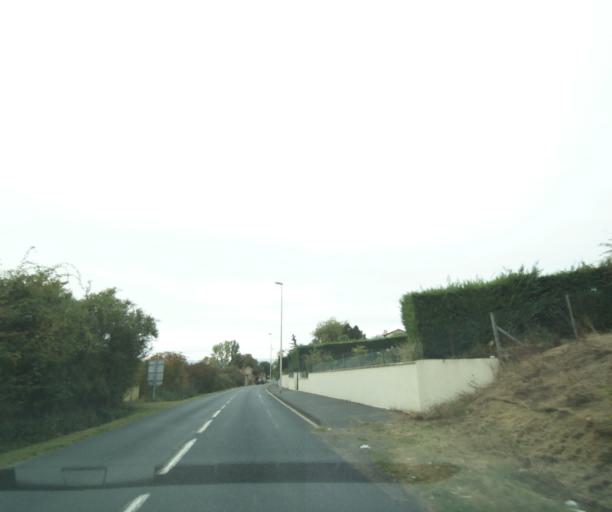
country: FR
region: Auvergne
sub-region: Departement du Puy-de-Dome
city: Gerzat
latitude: 45.8398
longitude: 3.1535
